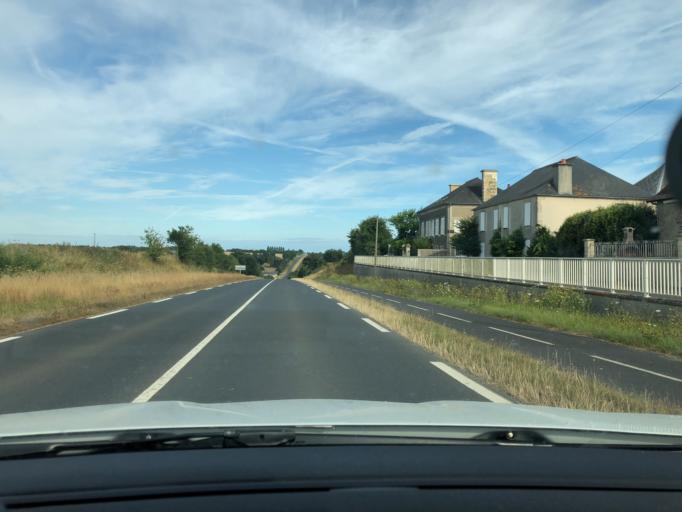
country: FR
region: Lower Normandy
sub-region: Departement du Calvados
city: Saint-Vigor-le-Grand
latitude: 49.2494
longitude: -0.6259
